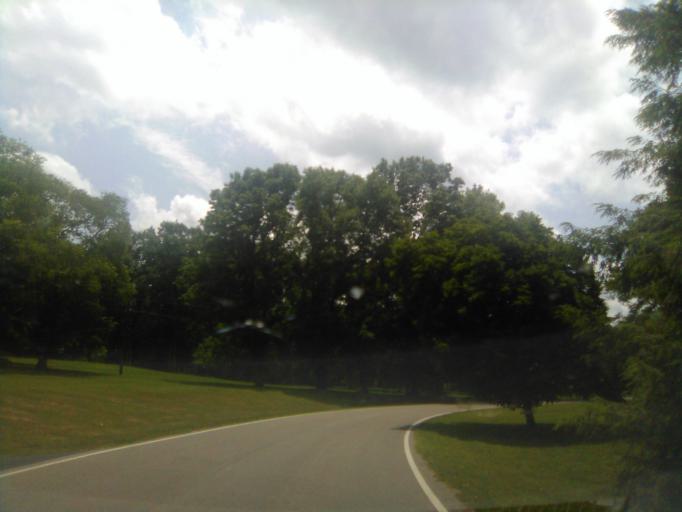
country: US
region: Tennessee
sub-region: Davidson County
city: Belle Meade
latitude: 36.0852
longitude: -86.8596
